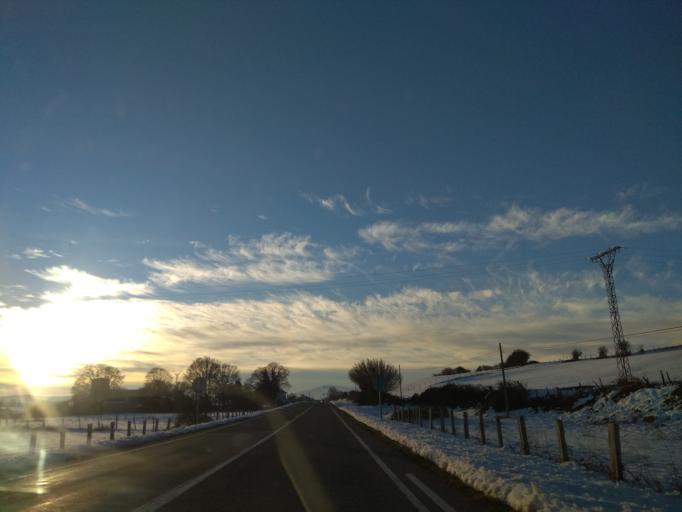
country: ES
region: Cantabria
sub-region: Provincia de Cantabria
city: San Miguel de Aguayo
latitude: 43.0173
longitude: -3.9977
